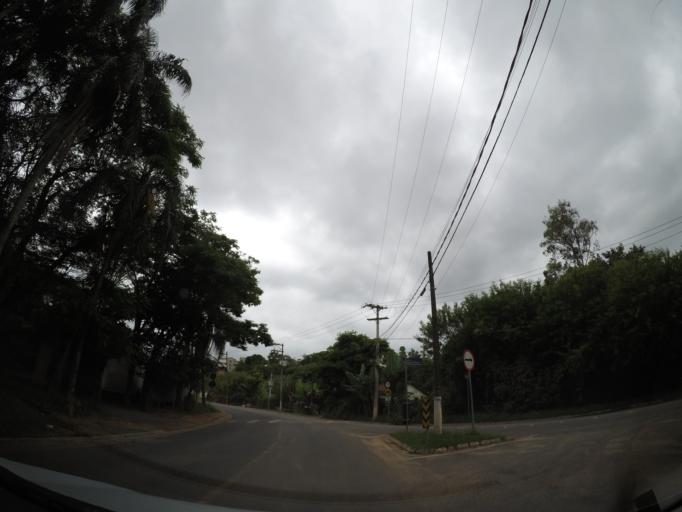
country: BR
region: Sao Paulo
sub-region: Louveira
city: Louveira
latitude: -23.0937
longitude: -46.9840
